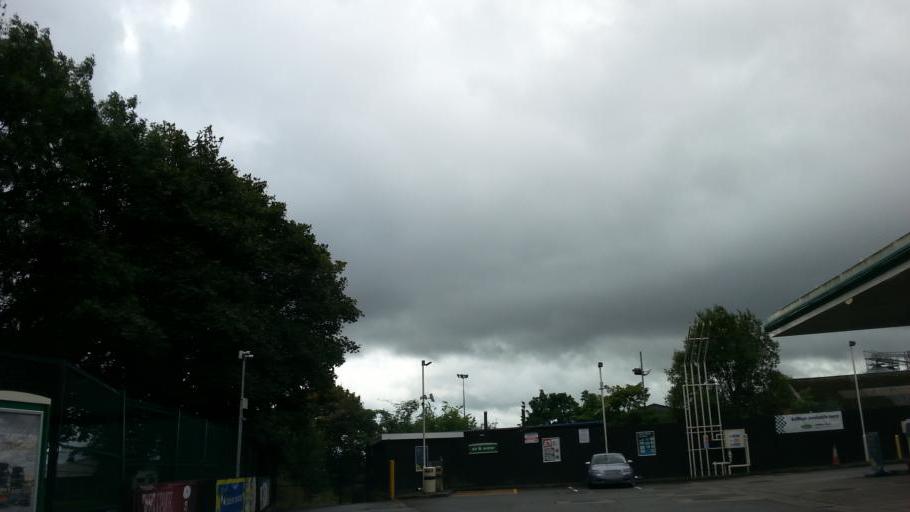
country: GB
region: England
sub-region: Sandwell
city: Smethwick
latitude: 52.5106
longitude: -1.9688
